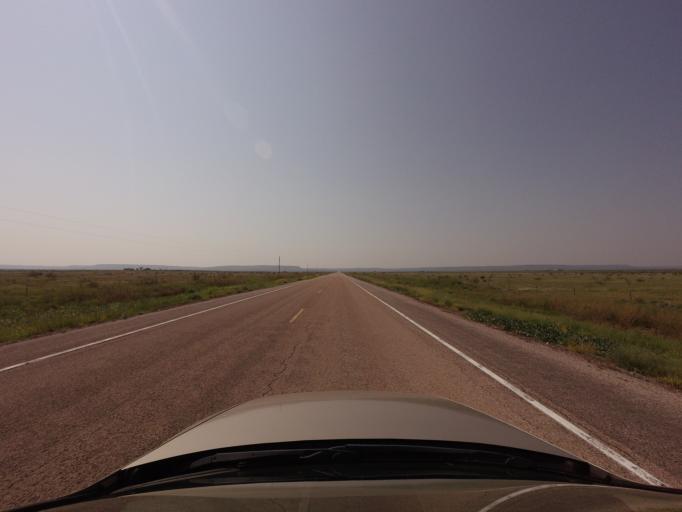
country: US
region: New Mexico
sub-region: Quay County
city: Tucumcari
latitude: 34.9013
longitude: -103.7603
